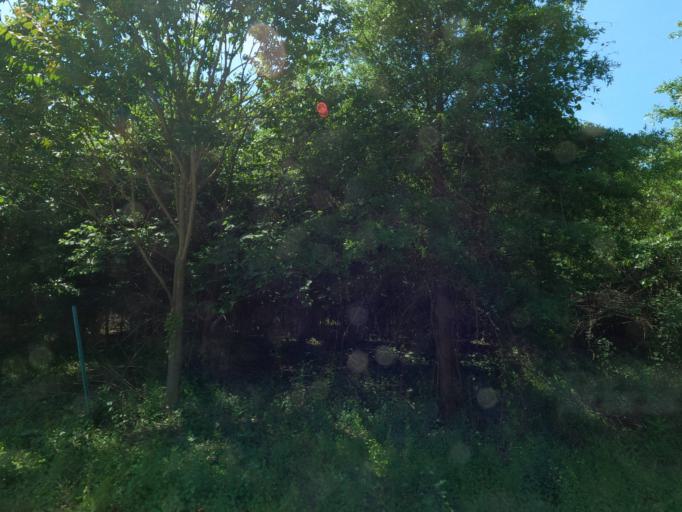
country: US
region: Maryland
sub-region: Howard County
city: Savage
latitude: 39.1822
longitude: -76.8240
